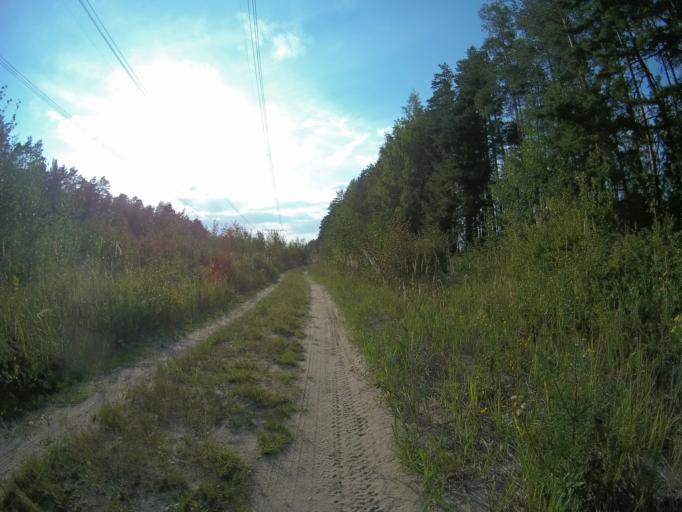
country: RU
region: Vladimir
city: Kommunar
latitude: 56.0609
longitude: 40.4460
